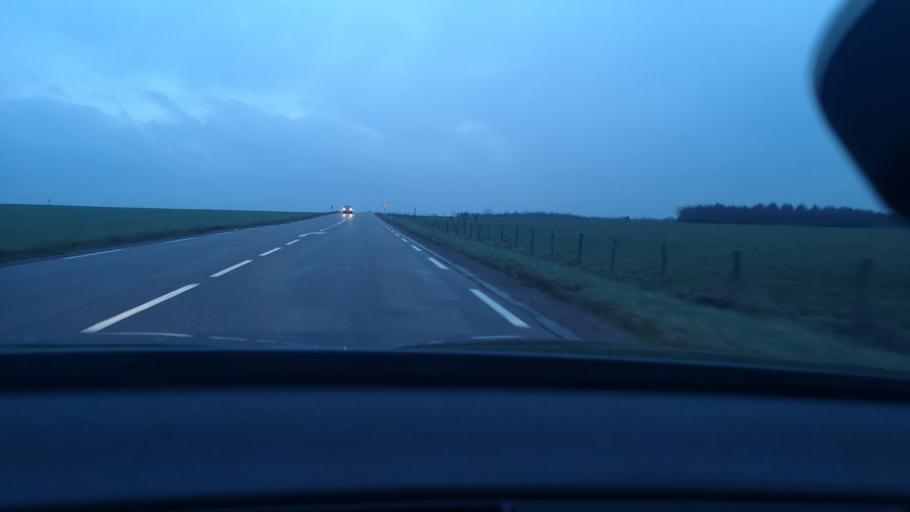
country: FR
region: Bourgogne
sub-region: Departement de Saone-et-Loire
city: Verdun-sur-le-Doubs
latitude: 47.0086
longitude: 4.9655
